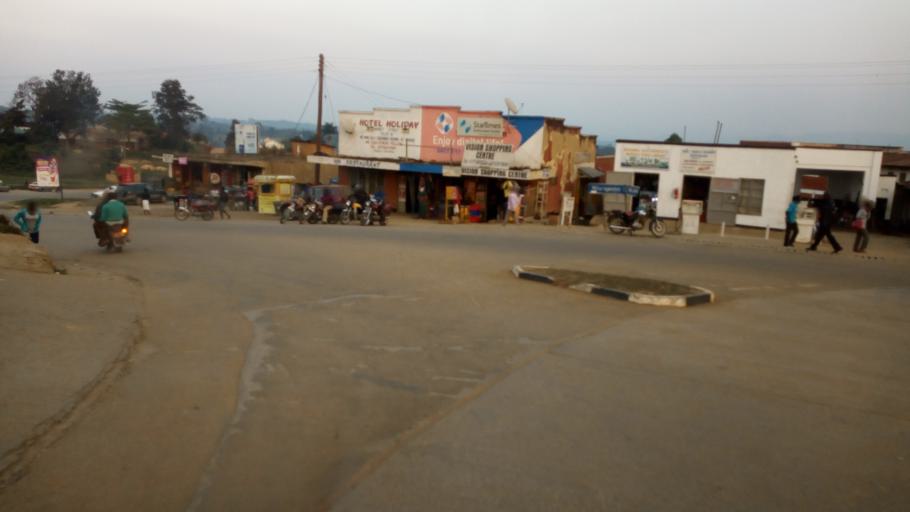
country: UG
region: Western Region
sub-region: Rukungiri District
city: Rukungiri
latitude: -0.7908
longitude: 29.9266
